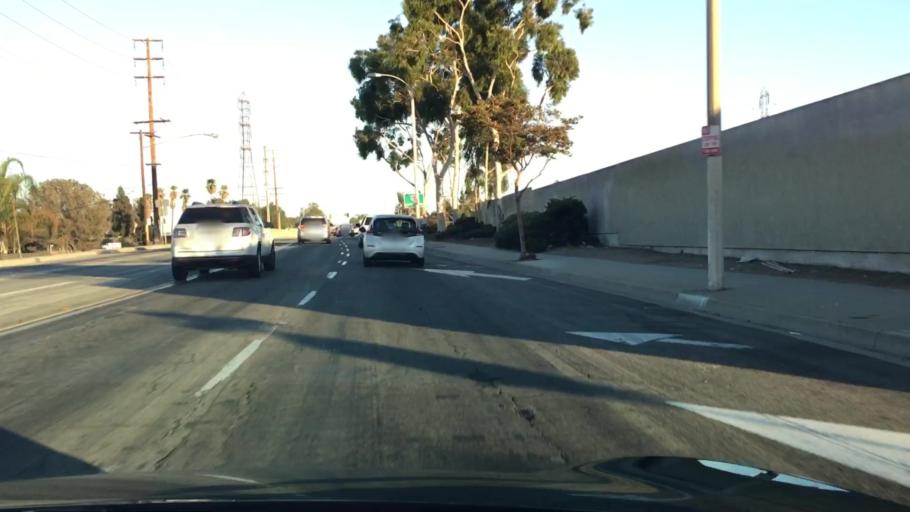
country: US
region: California
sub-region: Los Angeles County
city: Santa Fe Springs
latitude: 33.9511
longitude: -118.0955
